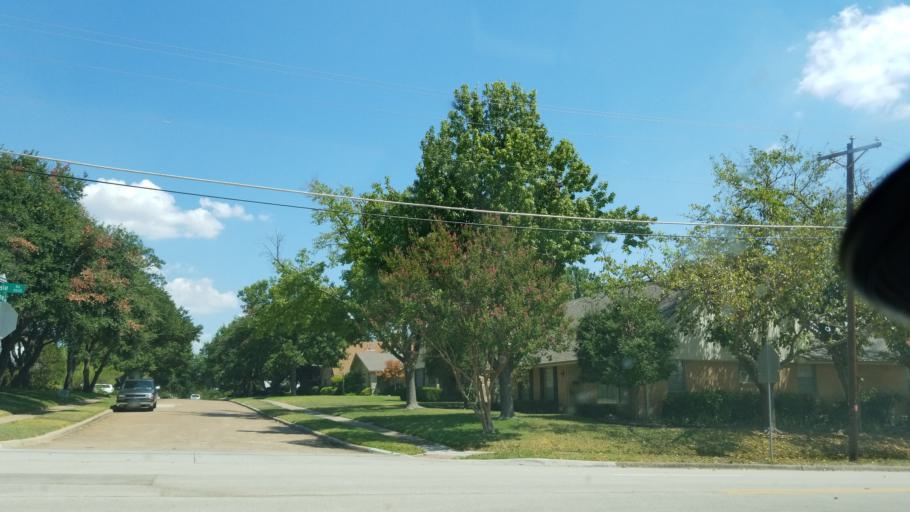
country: US
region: Texas
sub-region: Dallas County
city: Richardson
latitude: 32.8821
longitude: -96.7093
